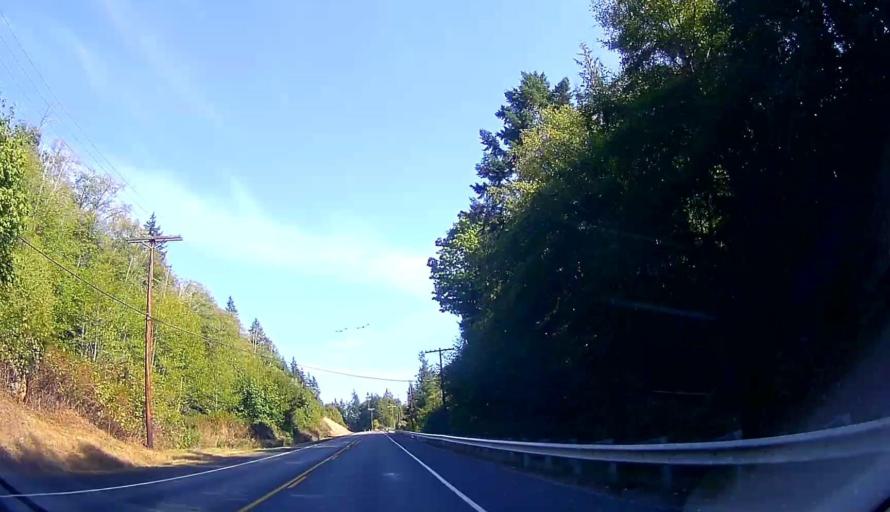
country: US
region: Washington
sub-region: Island County
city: Camano
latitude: 48.1907
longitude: -122.4978
